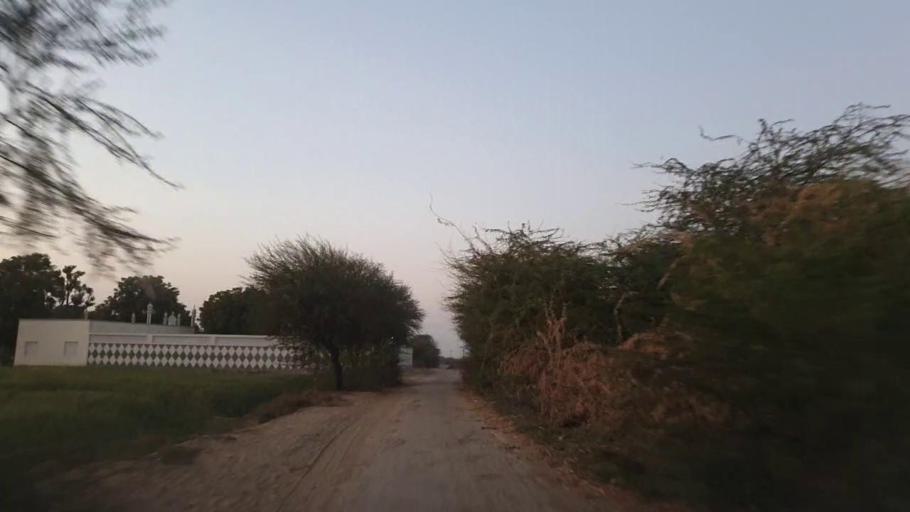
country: PK
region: Sindh
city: Naukot
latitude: 24.8874
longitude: 69.3854
